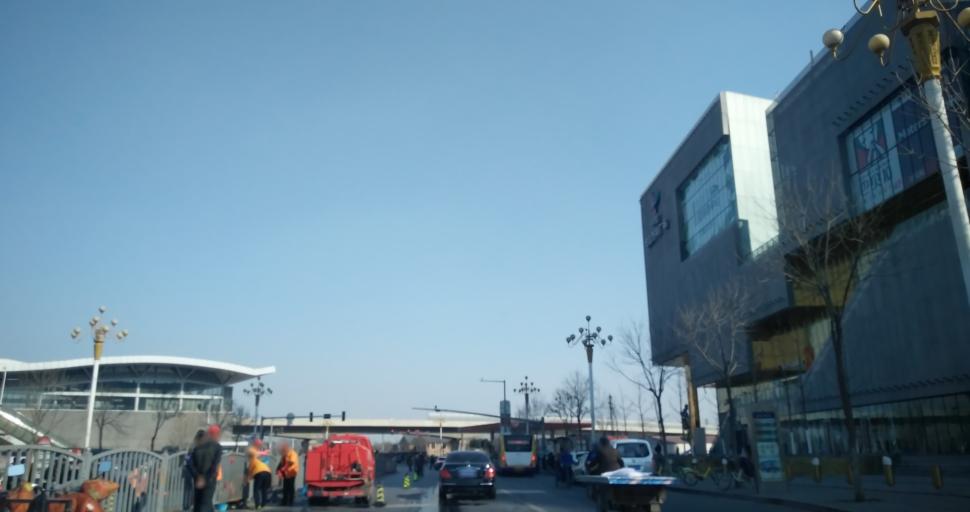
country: CN
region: Beijing
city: Jiugong
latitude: 39.8051
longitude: 116.4528
